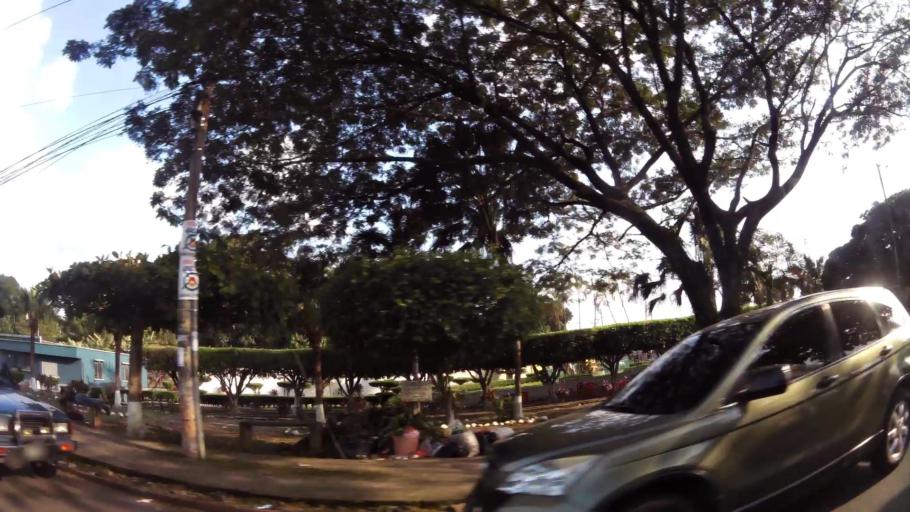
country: GT
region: Retalhuleu
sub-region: Municipio de Retalhuleu
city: Retalhuleu
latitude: 14.5407
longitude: -91.6758
